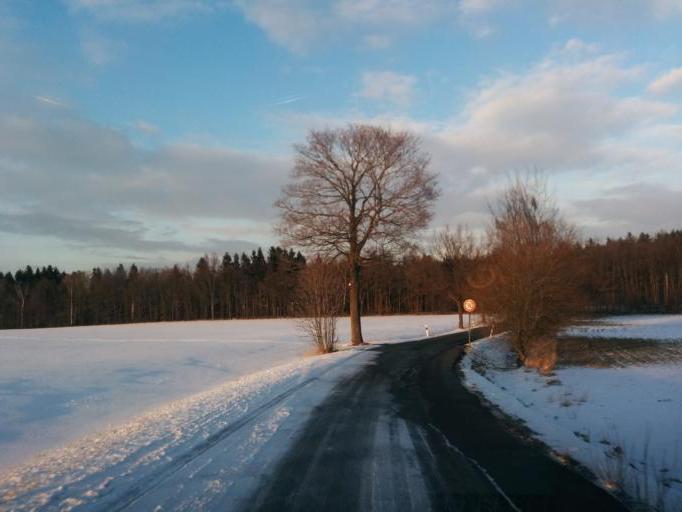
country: DE
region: Saxony
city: Niederwiesa
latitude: 50.8426
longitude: 13.0348
